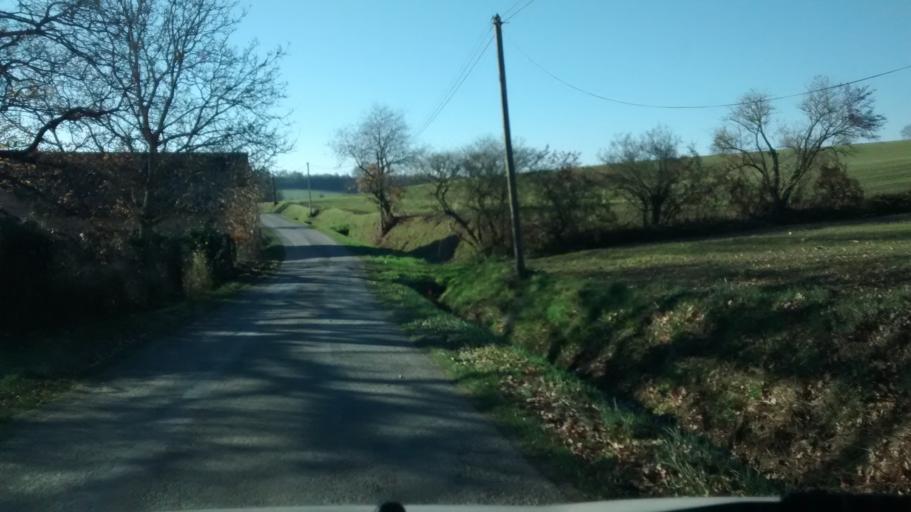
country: FR
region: Brittany
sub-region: Departement d'Ille-et-Vilaine
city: La Bouexiere
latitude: 48.1999
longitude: -1.4628
